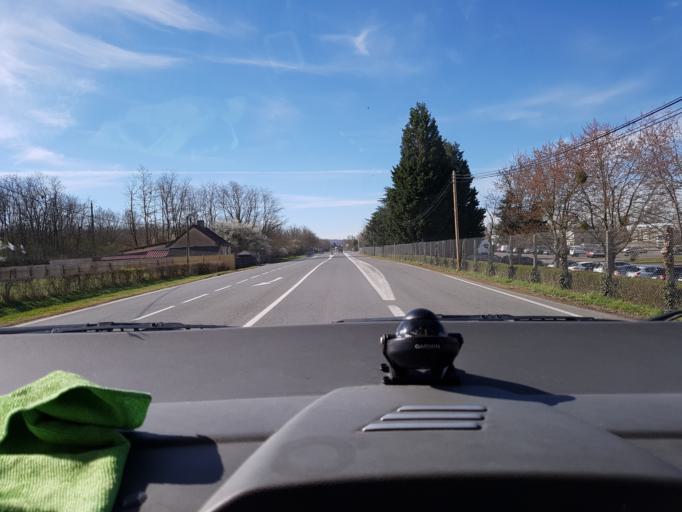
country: FR
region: Bourgogne
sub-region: Departement de Saone-et-Loire
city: Gueugnon
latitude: 46.5815
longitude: 4.0622
